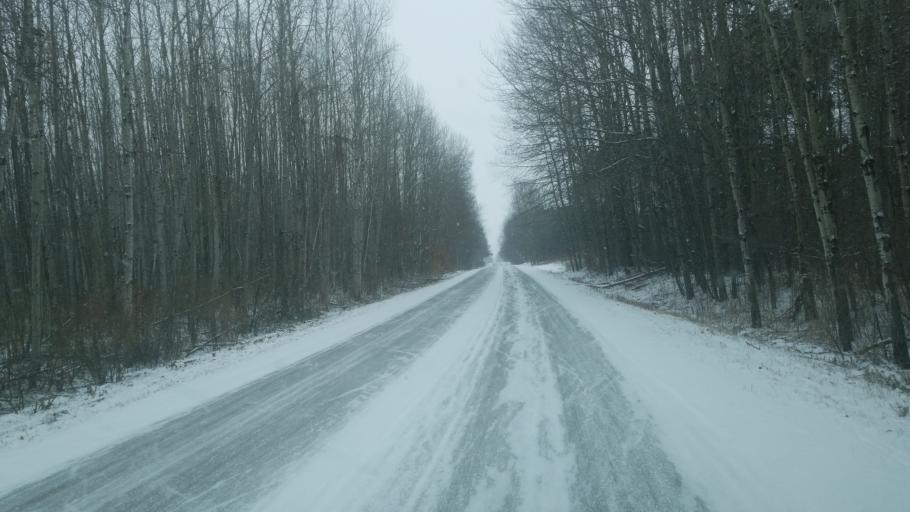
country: US
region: Michigan
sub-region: Mecosta County
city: Big Rapids
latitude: 43.7383
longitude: -85.4035
